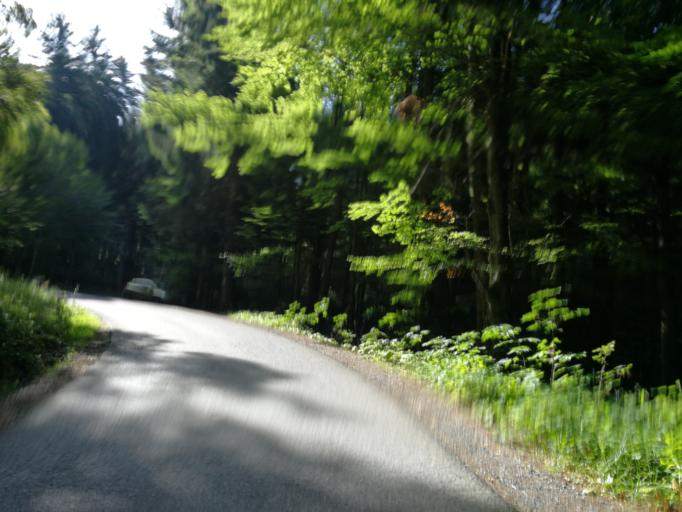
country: CH
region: Saint Gallen
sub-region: Wahlkreis See-Gaster
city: Gommiswald
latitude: 47.2519
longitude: 9.0406
